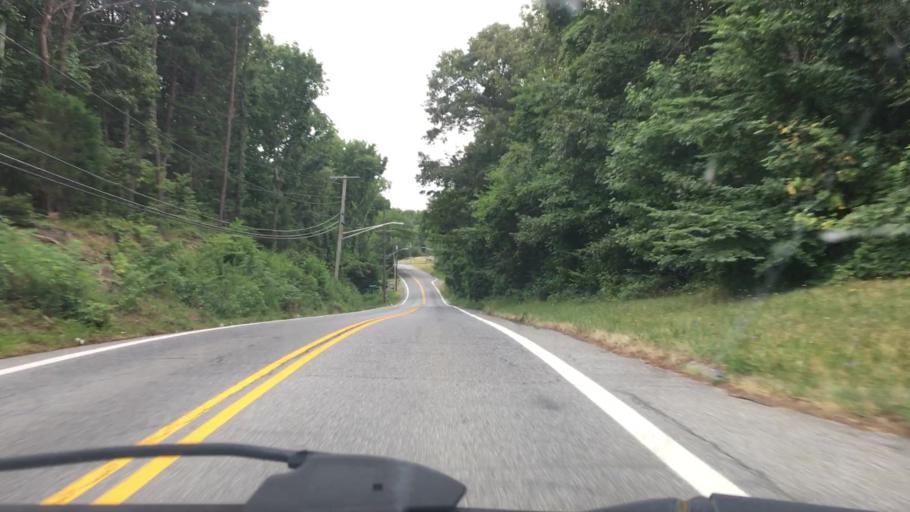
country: US
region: Maryland
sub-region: Prince George's County
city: Glenn Dale
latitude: 39.0204
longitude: -76.7851
